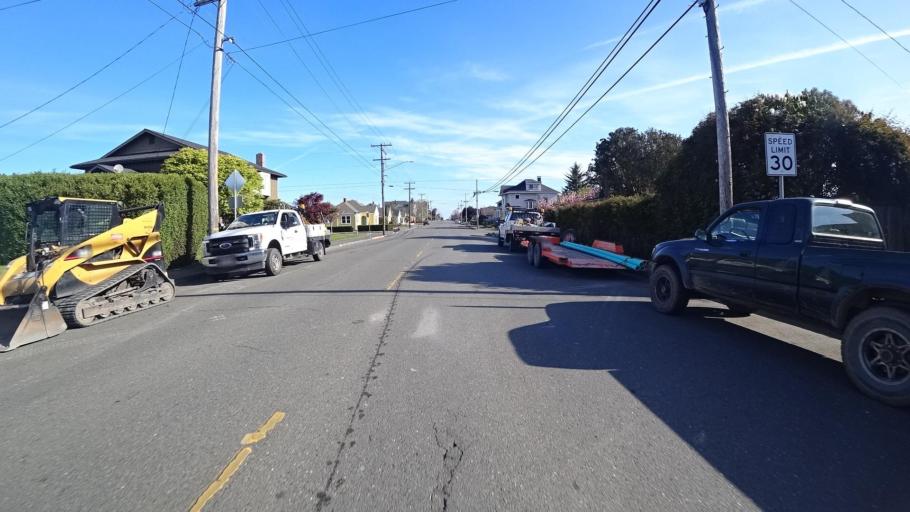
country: US
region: California
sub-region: Humboldt County
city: Eureka
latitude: 40.7836
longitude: -124.1646
